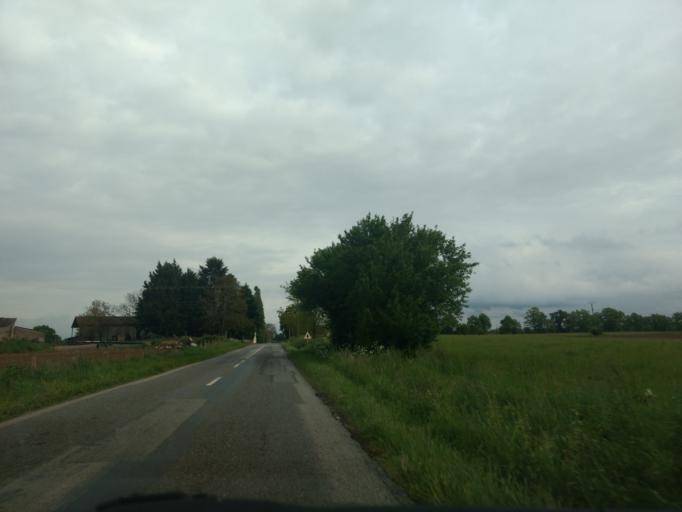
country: FR
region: Midi-Pyrenees
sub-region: Departement de l'Aveyron
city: Viviez
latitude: 44.5175
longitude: 2.1827
